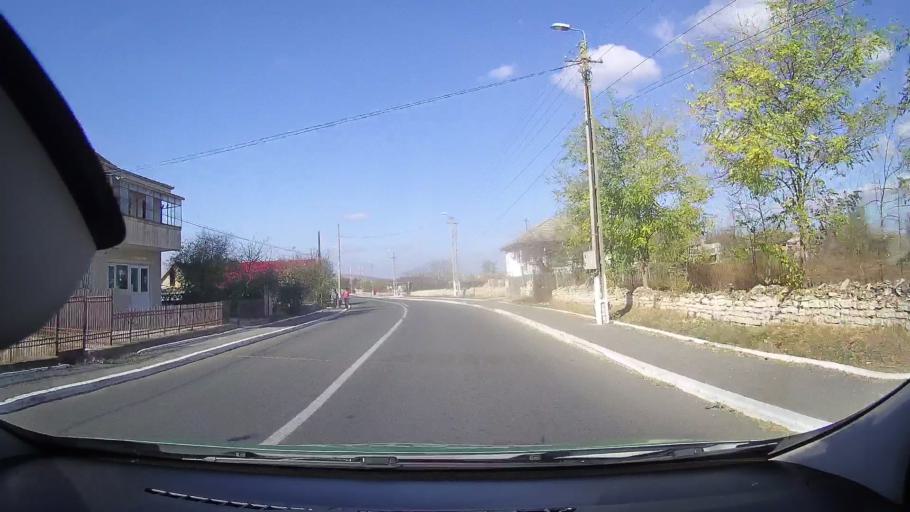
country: RO
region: Tulcea
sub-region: Comuna Ceamurlia de Jos
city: Ceamurlia de Jos
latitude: 44.7434
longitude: 28.7226
